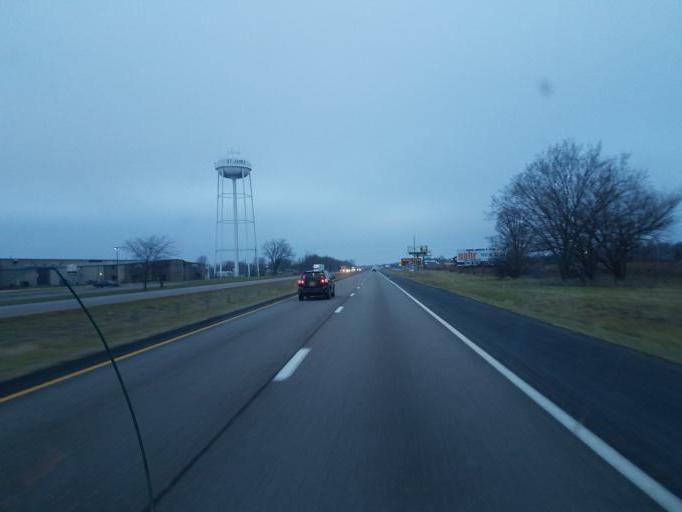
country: US
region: Missouri
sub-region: Phelps County
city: Saint James
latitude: 38.0112
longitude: -91.6009
